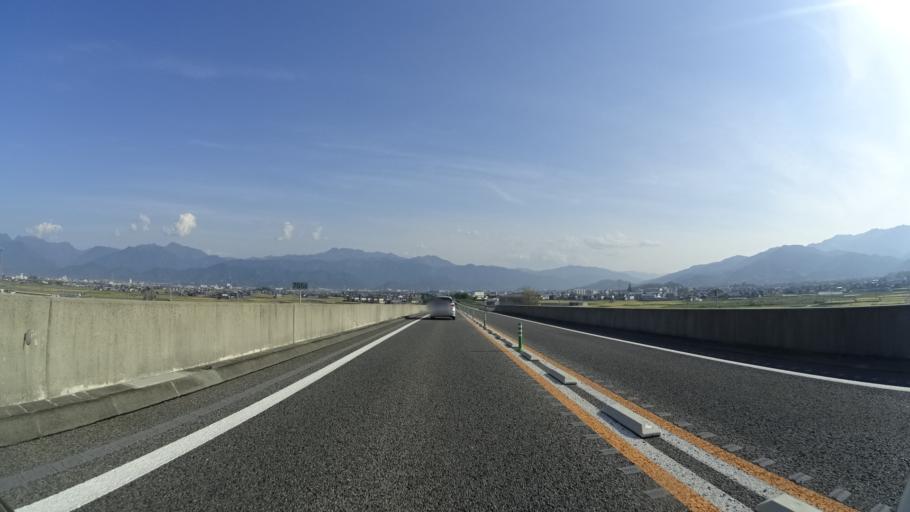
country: JP
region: Ehime
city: Saijo
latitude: 33.9482
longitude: 133.0692
